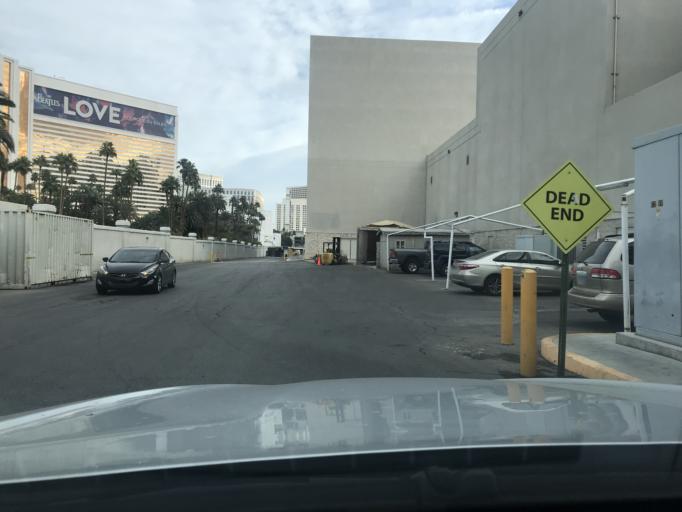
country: US
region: Nevada
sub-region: Clark County
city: Paradise
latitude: 36.1197
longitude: -115.1789
